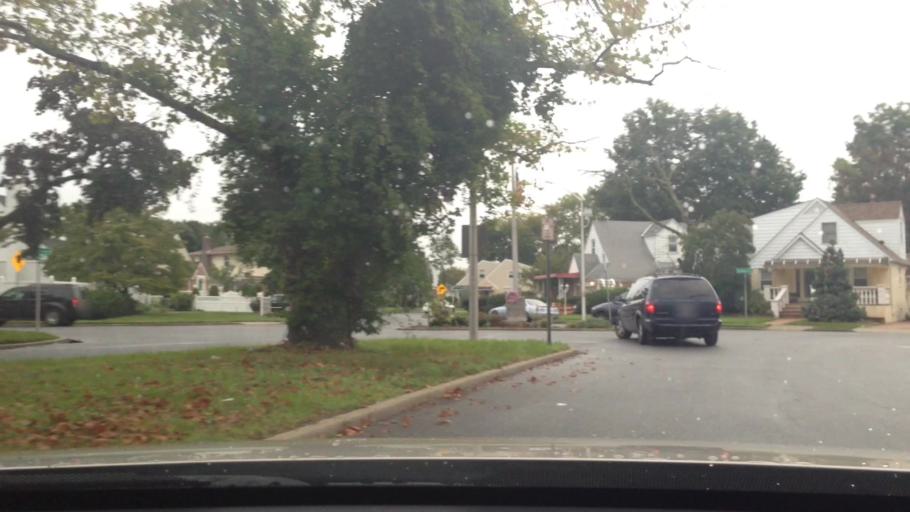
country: US
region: New York
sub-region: Nassau County
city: Elmont
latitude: 40.6883
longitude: -73.7179
